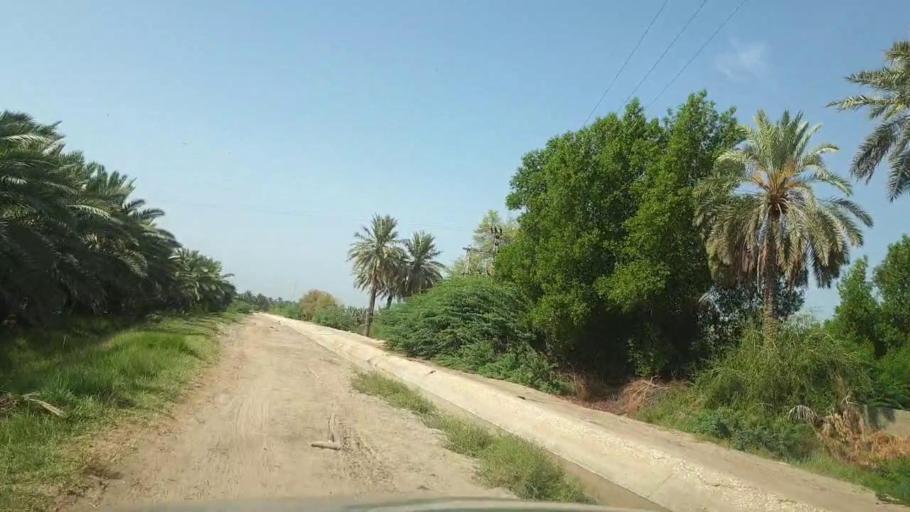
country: PK
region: Sindh
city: Rohri
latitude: 27.6542
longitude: 68.8793
